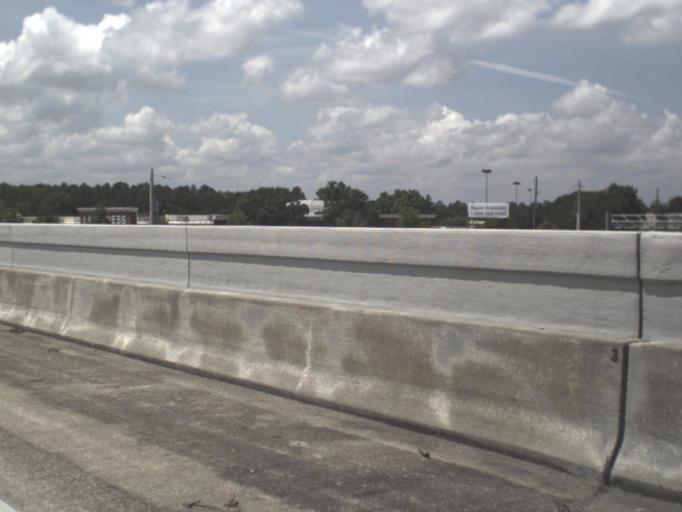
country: US
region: Florida
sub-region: Clay County
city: Bellair-Meadowbrook Terrace
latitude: 30.1968
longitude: -81.7394
